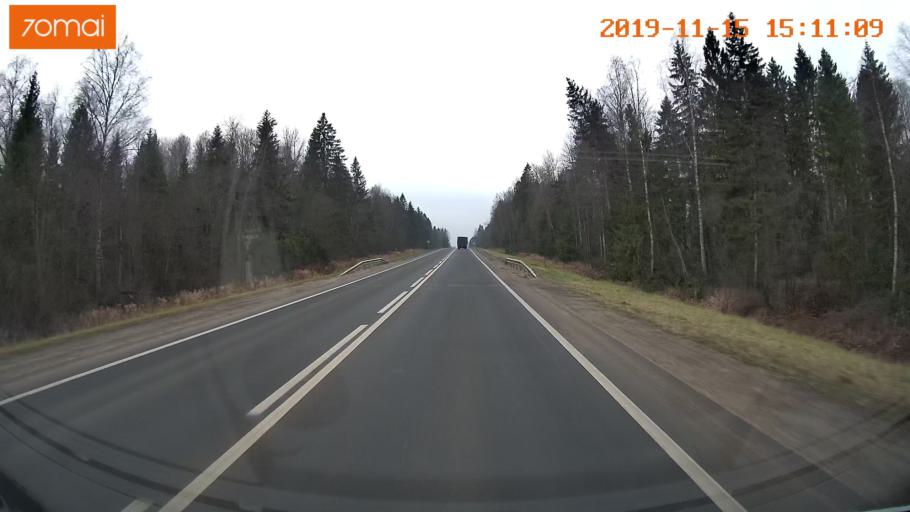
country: RU
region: Jaroslavl
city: Prechistoye
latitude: 58.3401
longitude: 40.2456
